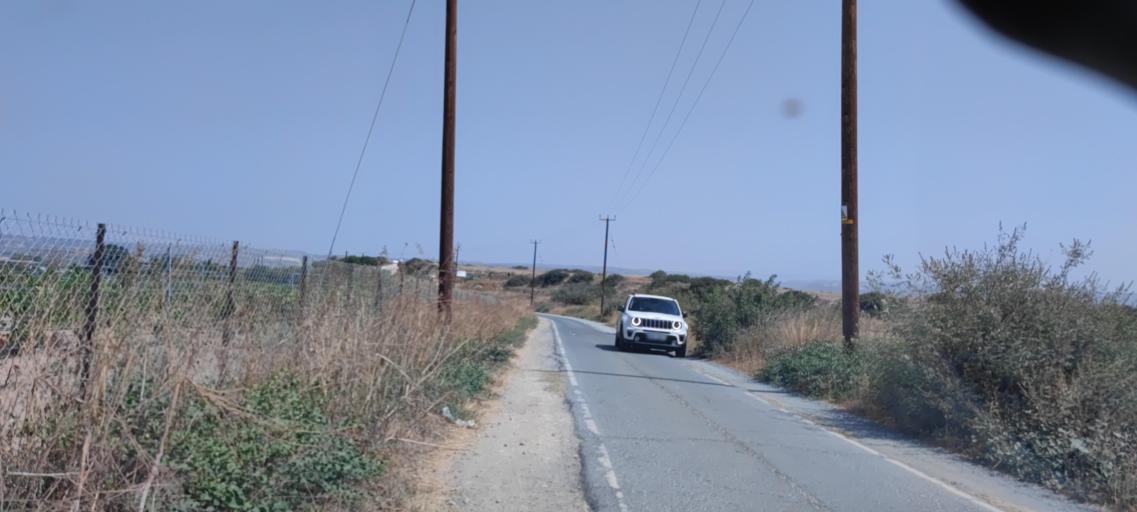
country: CY
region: Limassol
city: Pissouri
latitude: 34.6644
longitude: 32.7676
